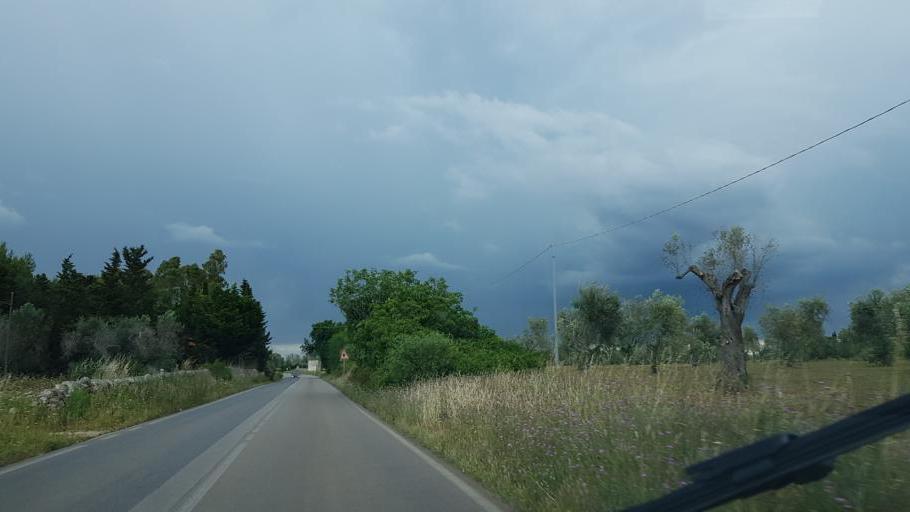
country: IT
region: Apulia
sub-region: Provincia di Lecce
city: Porto Cesareo
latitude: 40.3059
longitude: 17.8618
